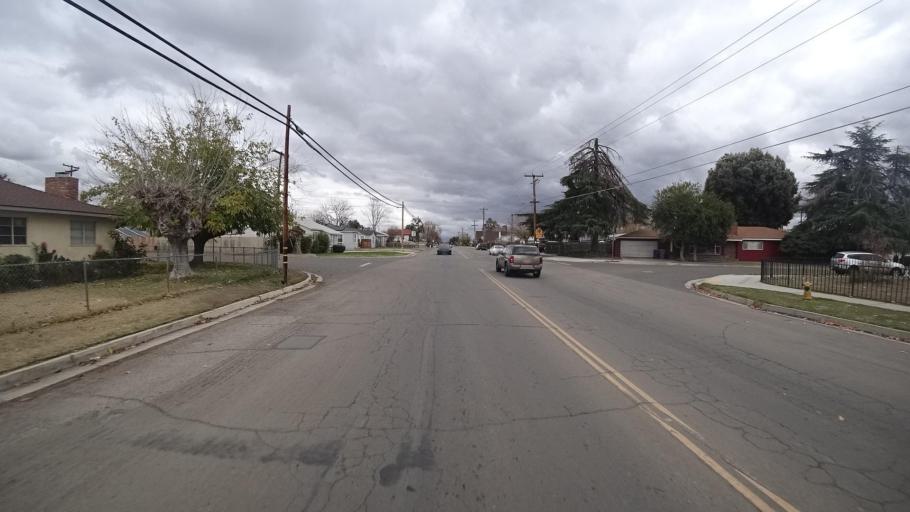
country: US
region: California
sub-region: Kern County
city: Bakersfield
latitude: 35.3467
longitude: -119.0326
